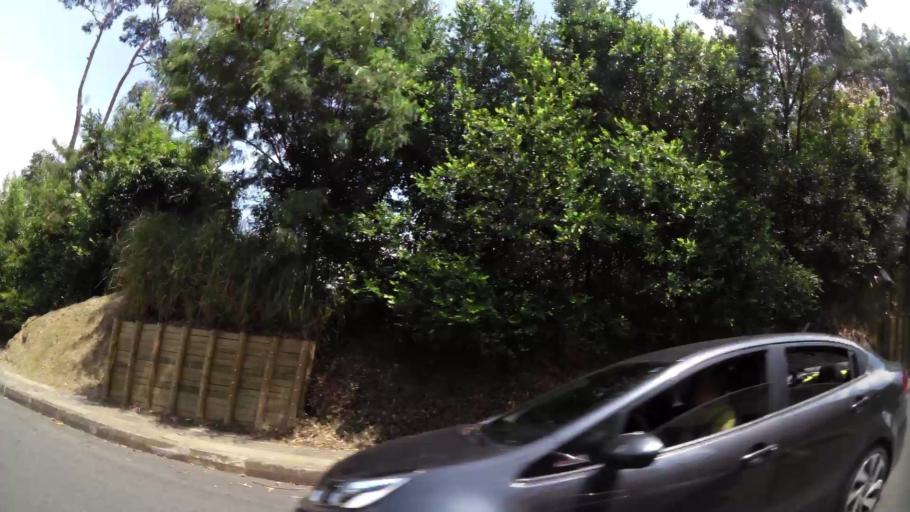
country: CO
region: Antioquia
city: Medellin
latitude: 6.2386
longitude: -75.6099
